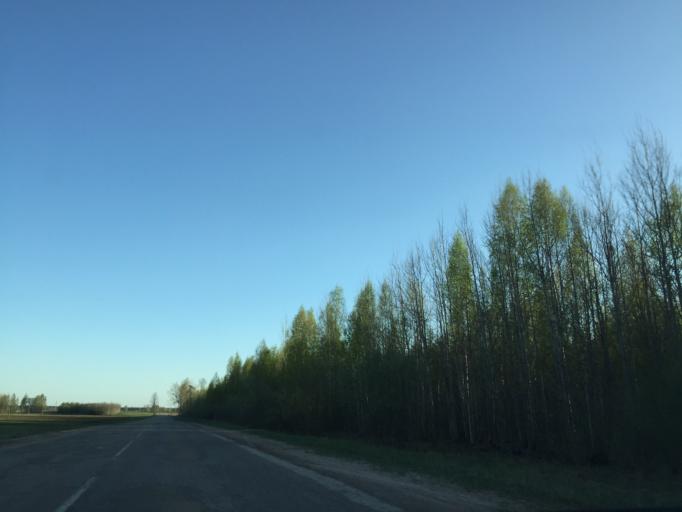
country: LV
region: Koknese
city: Koknese
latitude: 56.6997
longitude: 25.4879
